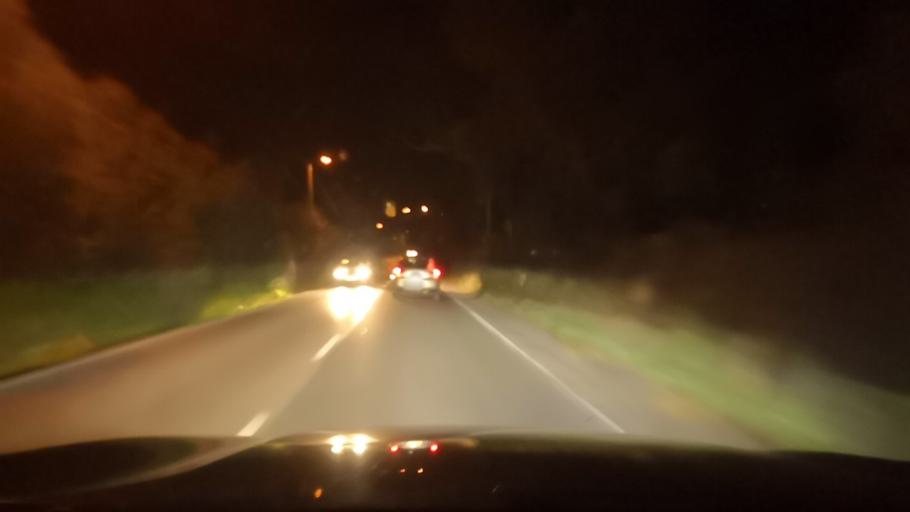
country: PT
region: Setubal
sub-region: Setubal
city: Setubal
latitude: 38.5426
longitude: -8.8625
